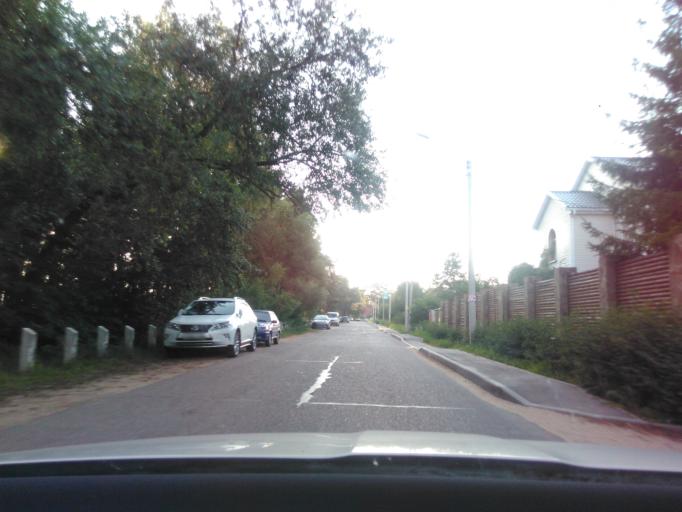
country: RU
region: Tverskaya
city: Konakovo
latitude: 56.7510
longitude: 36.7583
